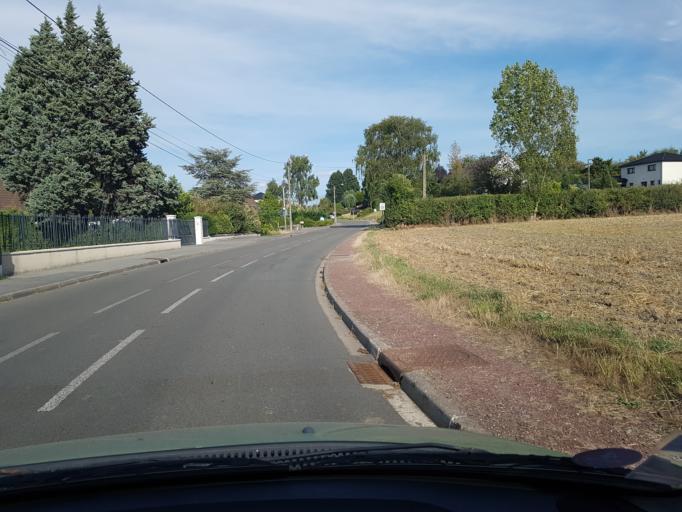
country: FR
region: Nord-Pas-de-Calais
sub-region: Departement du Pas-de-Calais
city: Labeuvriere
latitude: 50.5170
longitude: 2.5539
